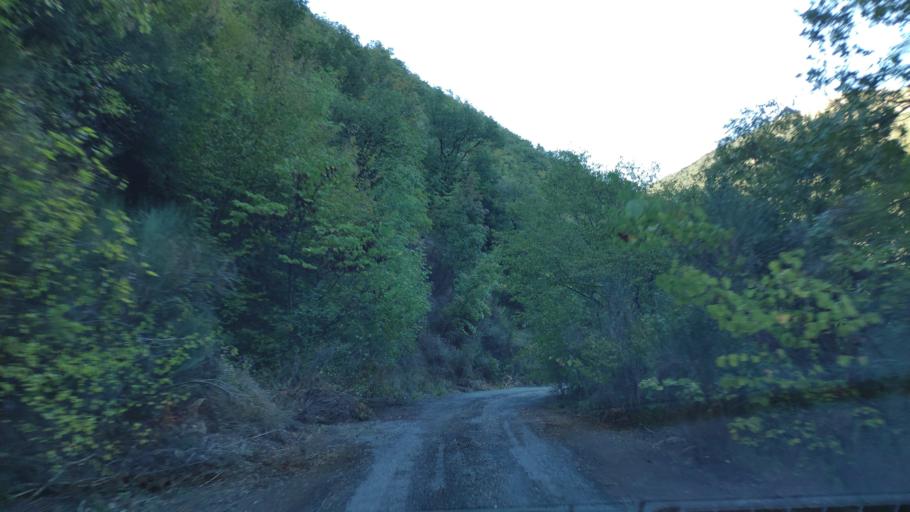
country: GR
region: Peloponnese
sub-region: Nomos Arkadias
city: Dimitsana
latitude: 37.5614
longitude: 22.0407
